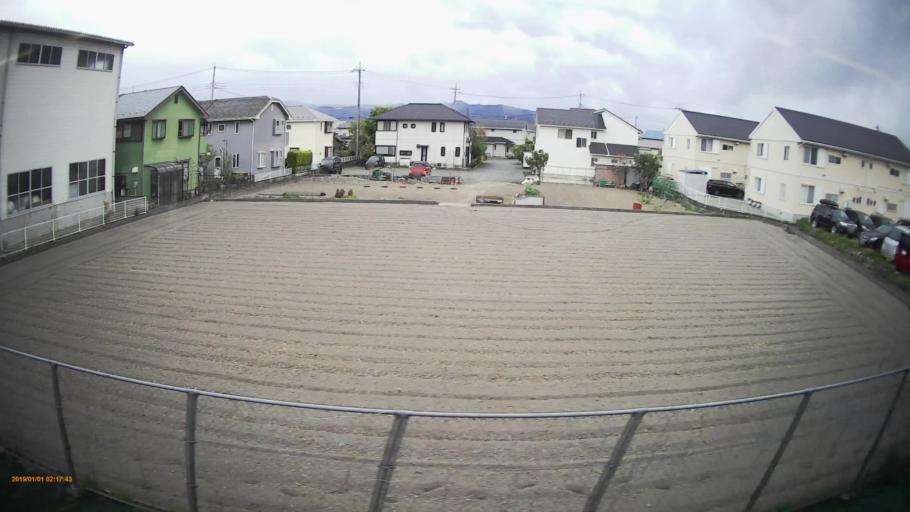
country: JP
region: Yamanashi
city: Ryuo
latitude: 35.6691
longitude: 138.5300
